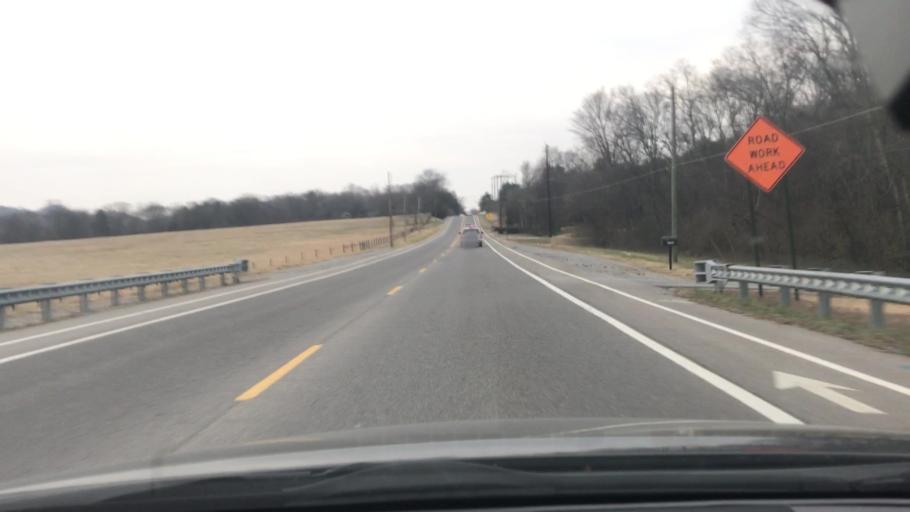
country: US
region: Tennessee
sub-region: Davidson County
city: Forest Hills
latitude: 36.0369
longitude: -86.8716
